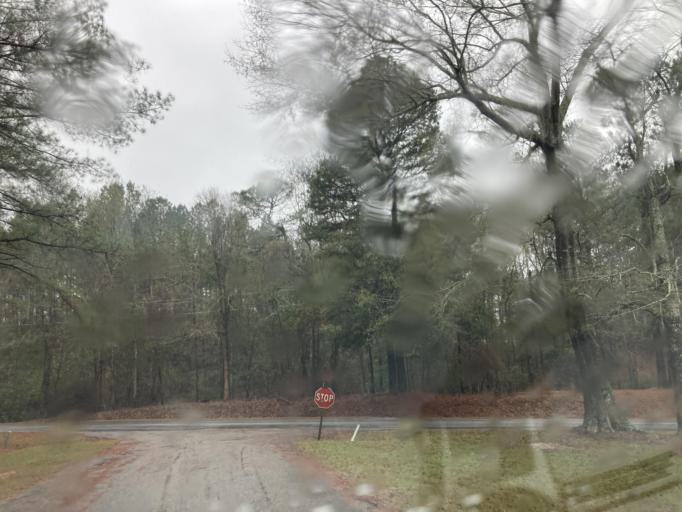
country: US
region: Mississippi
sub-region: Forrest County
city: Rawls Springs
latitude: 31.5025
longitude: -89.3433
